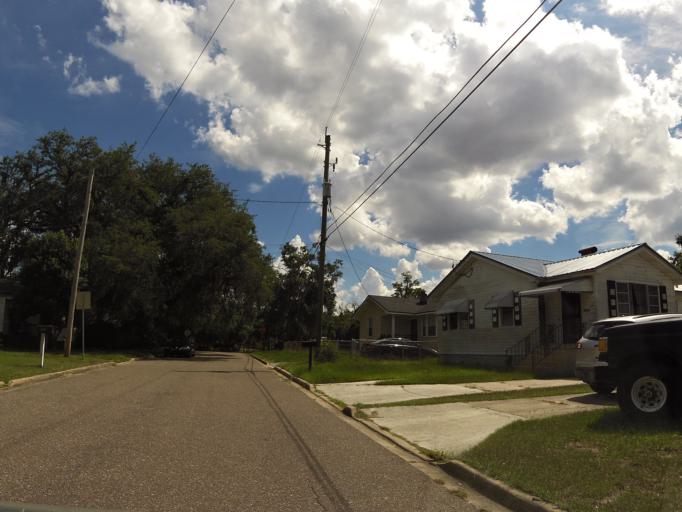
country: US
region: Florida
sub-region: Duval County
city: Jacksonville
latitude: 30.3870
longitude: -81.6468
